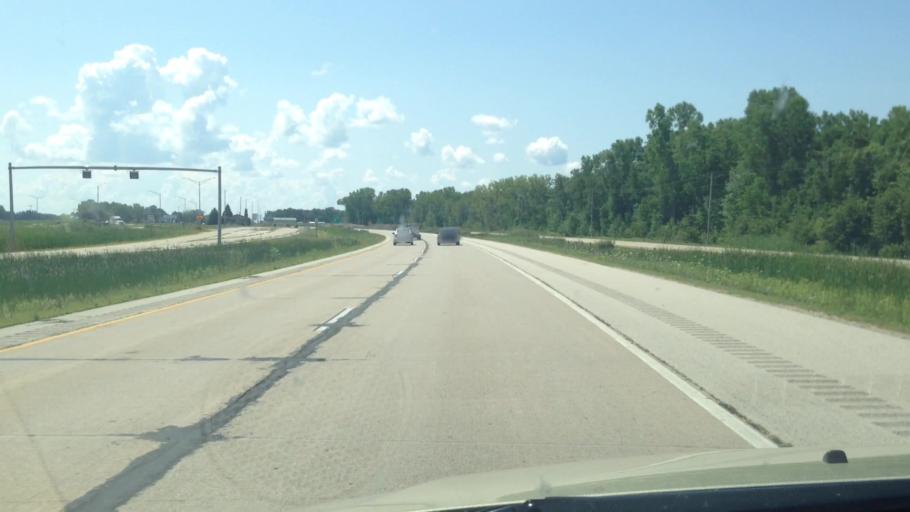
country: US
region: Wisconsin
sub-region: Brown County
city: Suamico
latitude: 44.7450
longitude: -88.0522
